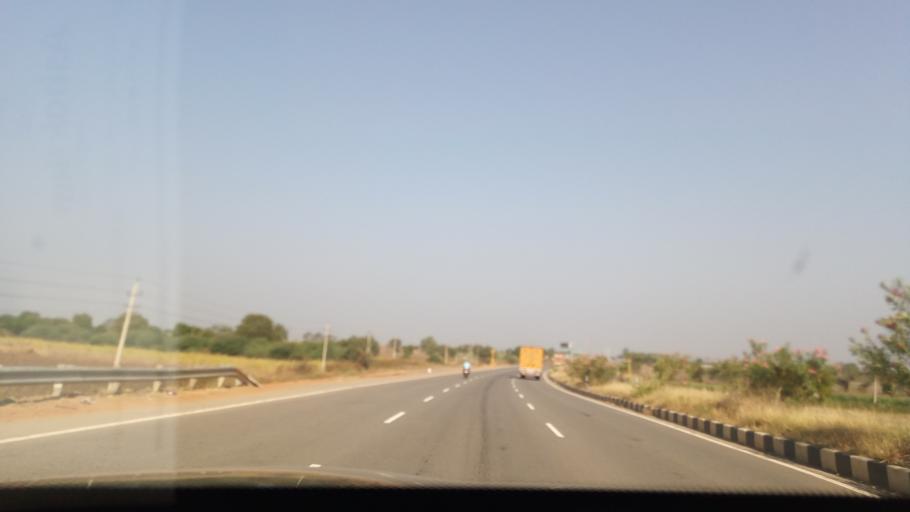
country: IN
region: Karnataka
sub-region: Haveri
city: Haveri
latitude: 14.7651
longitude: 75.4294
